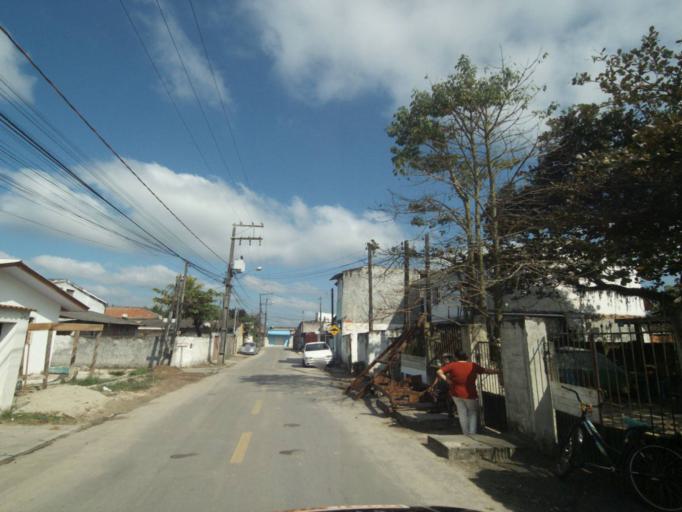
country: BR
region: Parana
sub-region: Paranagua
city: Paranagua
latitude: -25.5264
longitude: -48.5086
